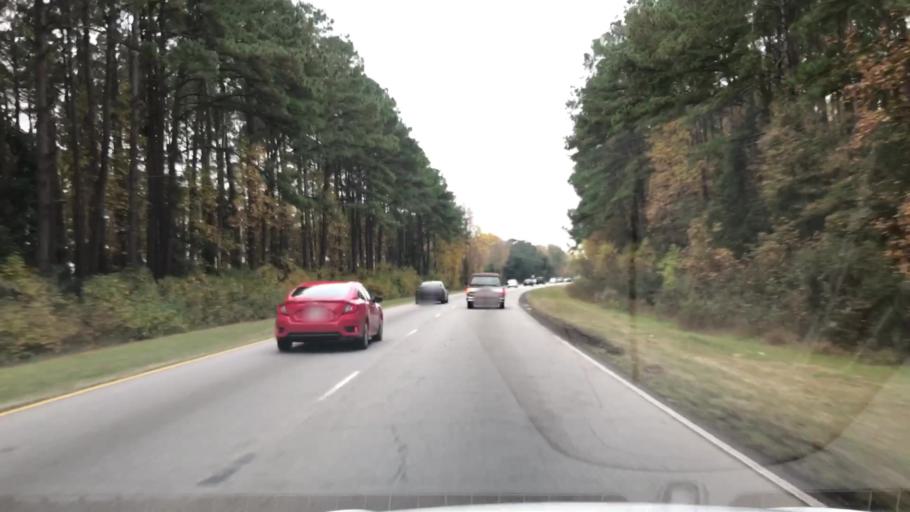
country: US
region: South Carolina
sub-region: Berkeley County
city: Goose Creek
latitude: 32.9482
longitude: -80.0439
